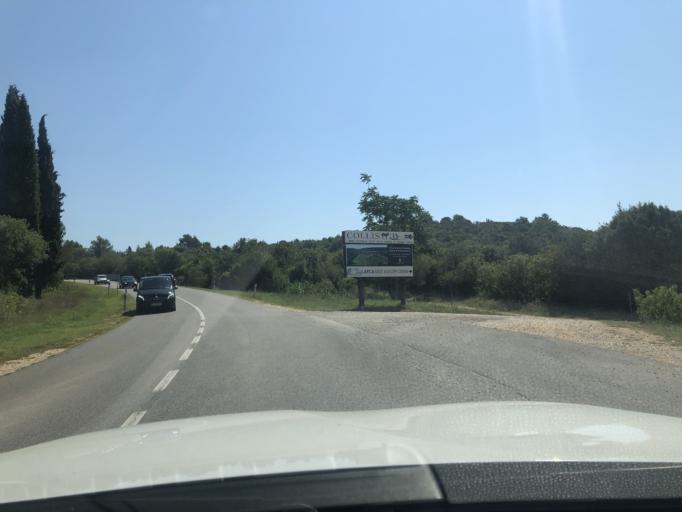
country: HR
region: Istarska
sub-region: Grad Rovinj
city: Rovinj
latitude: 45.0578
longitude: 13.7034
